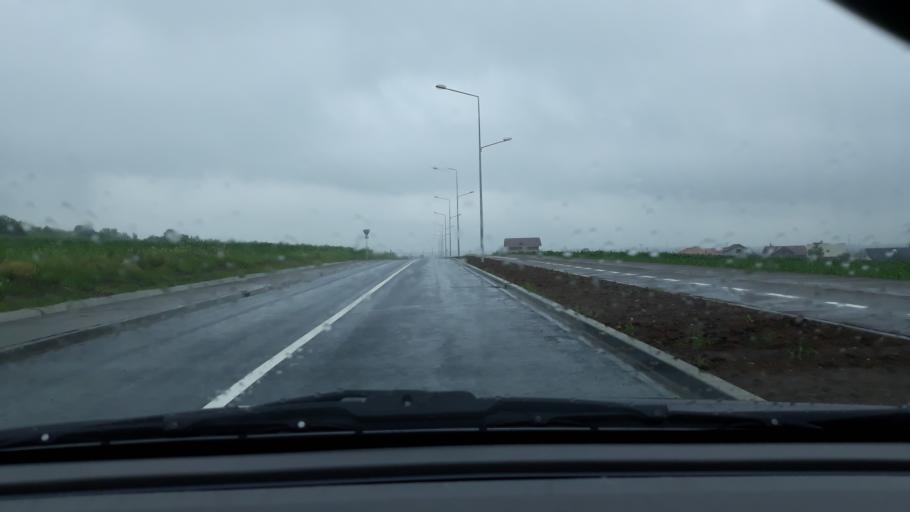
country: RO
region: Bihor
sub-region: Comuna Biharea
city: Biharea
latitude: 47.1082
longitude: 21.9063
